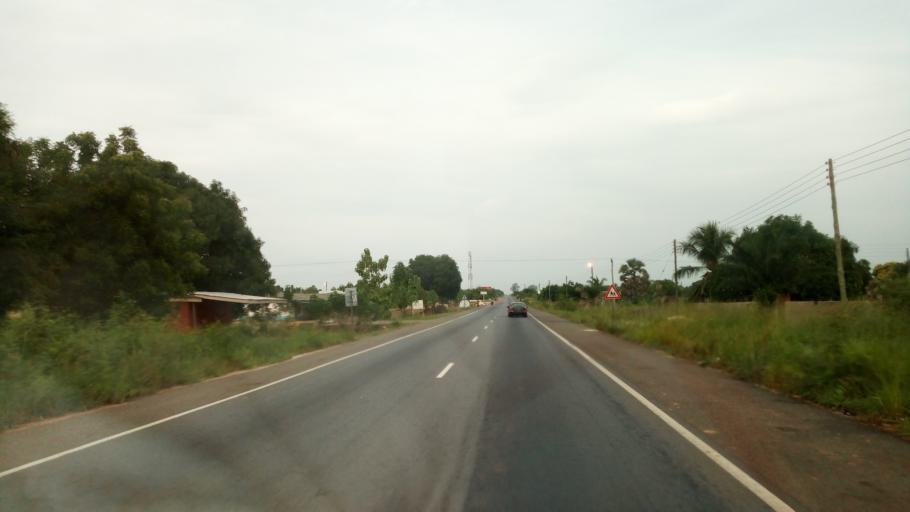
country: GH
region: Volta
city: Keta
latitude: 6.0656
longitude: 1.0113
